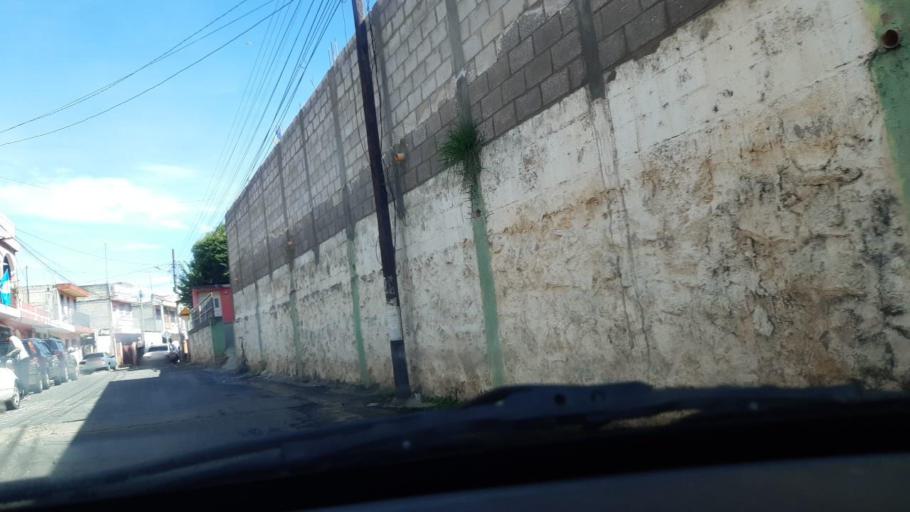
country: GT
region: Quetzaltenango
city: Salcaja
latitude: 14.8825
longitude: -91.4535
